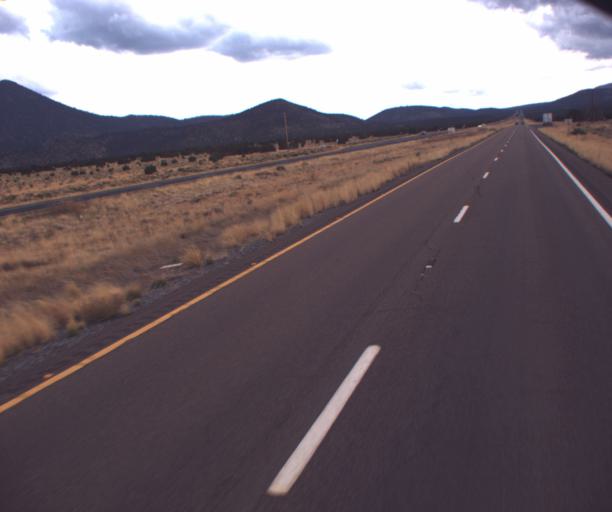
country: US
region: Arizona
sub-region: Coconino County
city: Flagstaff
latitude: 35.4435
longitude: -111.5652
